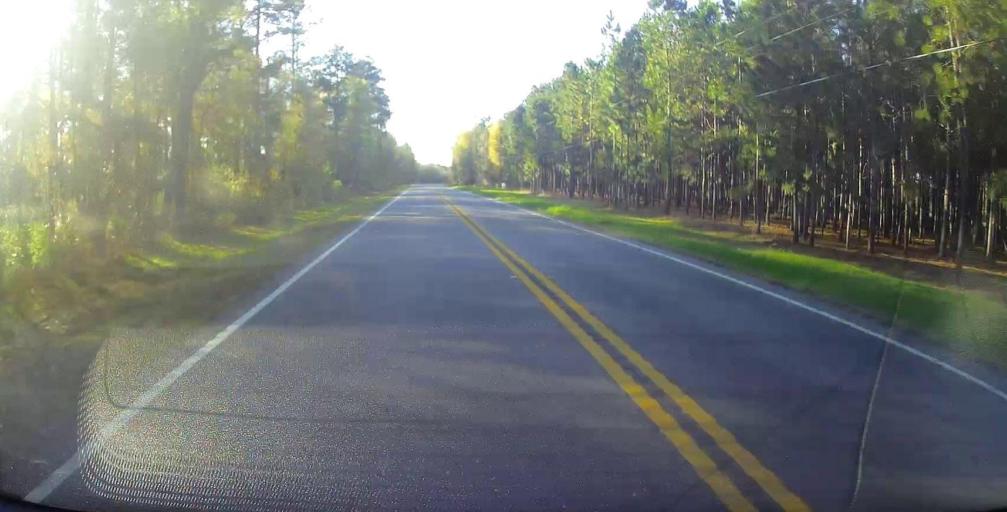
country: US
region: Georgia
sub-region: Pulaski County
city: Hawkinsville
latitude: 32.2656
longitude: -83.4283
